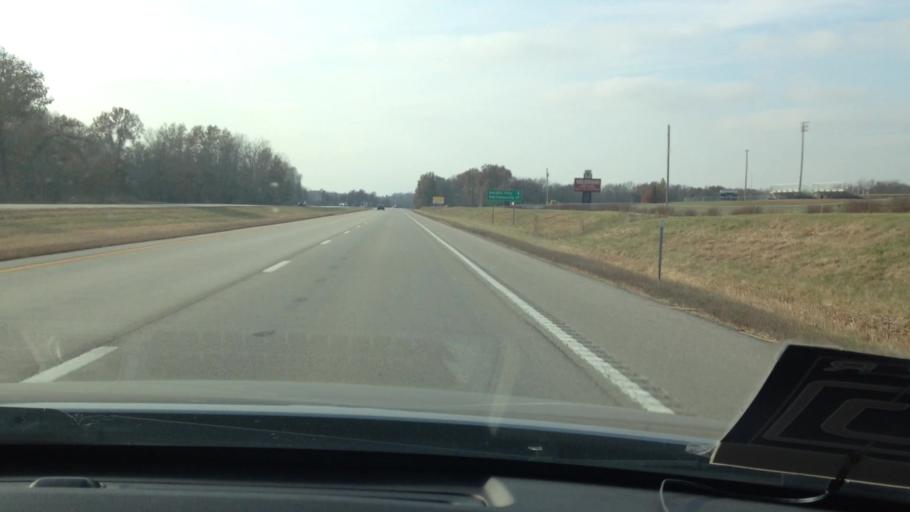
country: US
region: Missouri
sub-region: Cass County
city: Garden City
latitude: 38.5048
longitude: -94.0853
